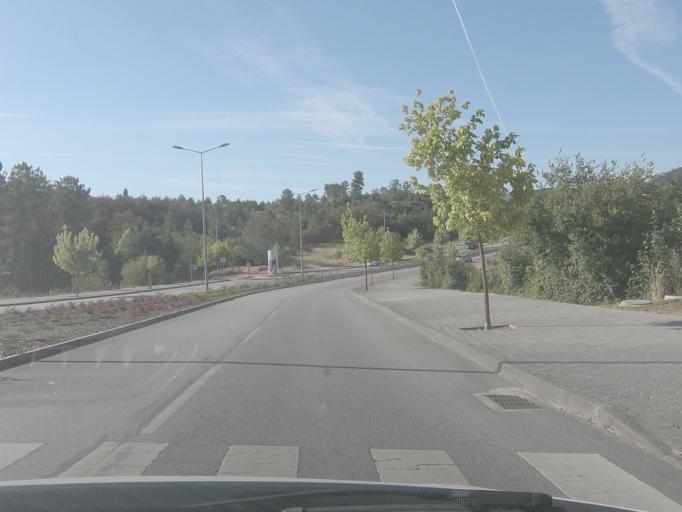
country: PT
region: Viseu
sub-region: Viseu
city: Abraveses
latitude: 40.6809
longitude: -7.9272
